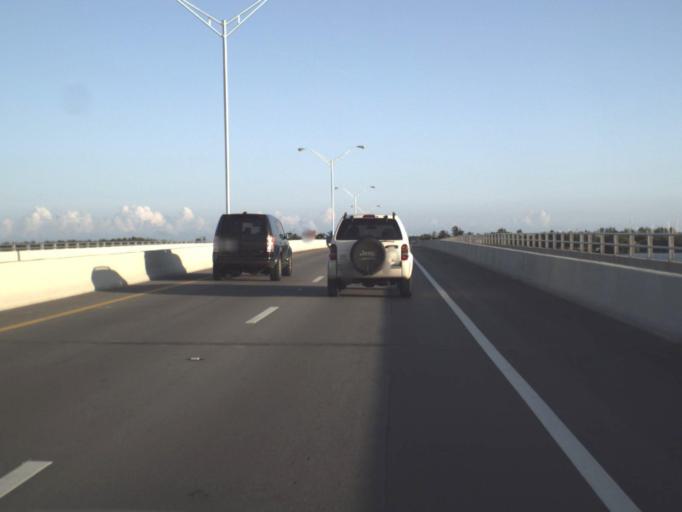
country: US
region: Florida
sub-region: Miami-Dade County
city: Key Biscayne
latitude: 25.7312
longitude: -80.1596
